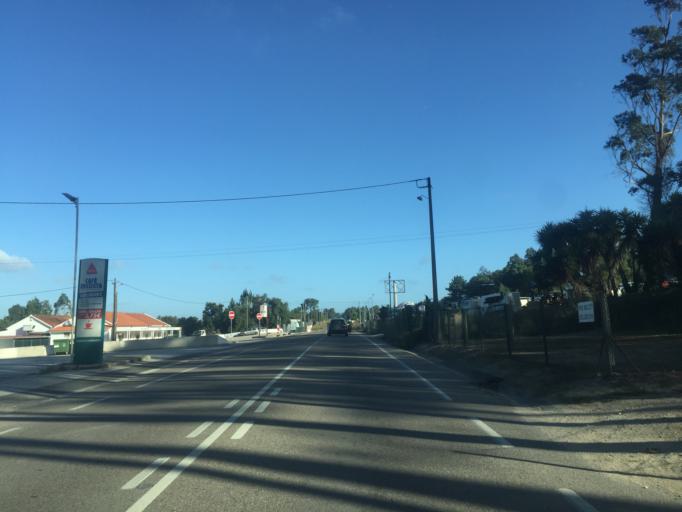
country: PT
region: Leiria
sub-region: Alcobaca
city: Benedita
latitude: 39.3815
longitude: -8.9618
